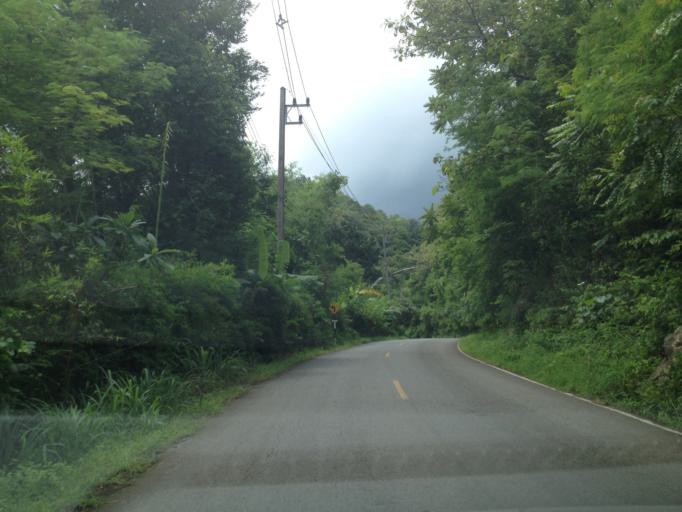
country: TH
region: Chiang Mai
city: Chiang Mai
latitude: 18.7615
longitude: 98.9203
